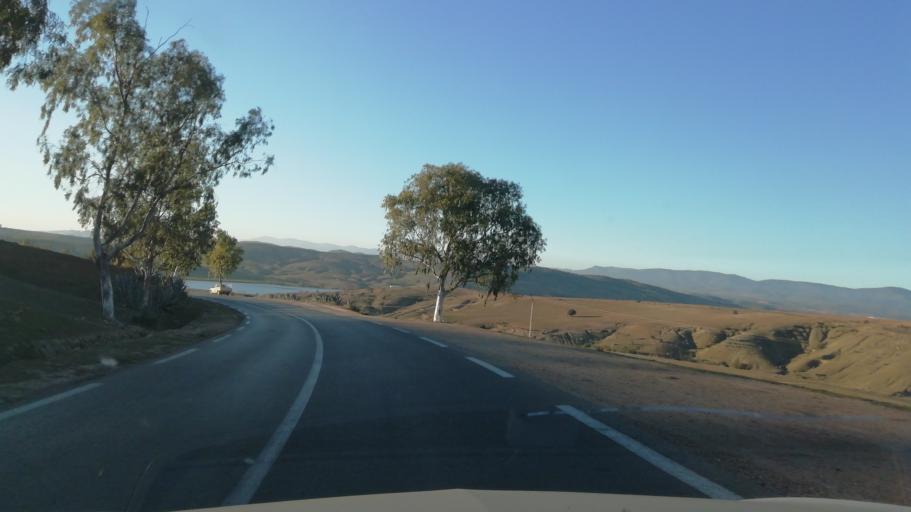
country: DZ
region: Tlemcen
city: Nedroma
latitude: 34.8278
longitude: -1.6399
